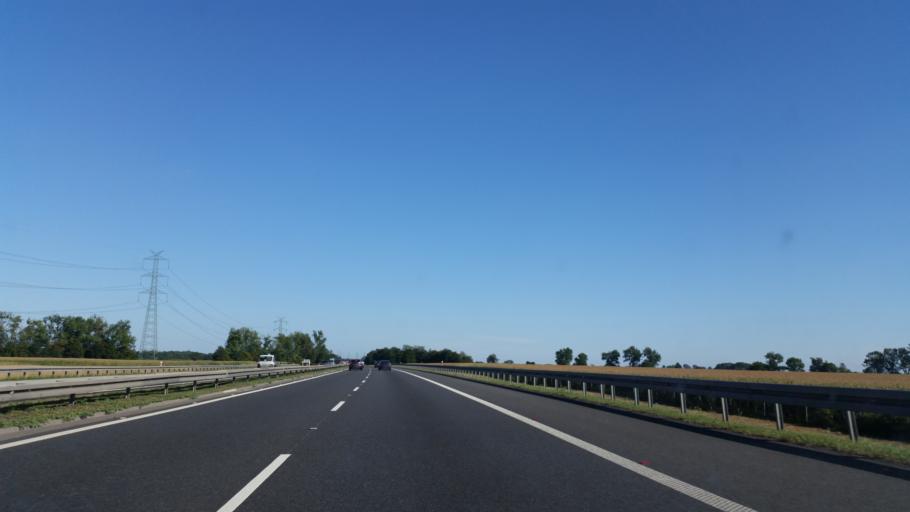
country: PL
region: Lower Silesian Voivodeship
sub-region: Powiat olawski
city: Wierzbno
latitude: 50.9156
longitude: 17.1428
